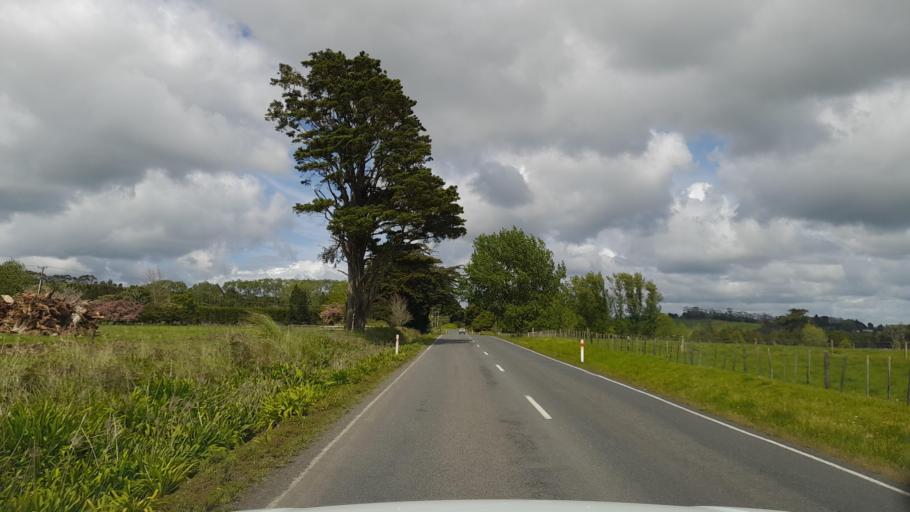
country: NZ
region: Northland
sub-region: Whangarei
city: Maungatapere
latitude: -35.6574
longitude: 174.1629
